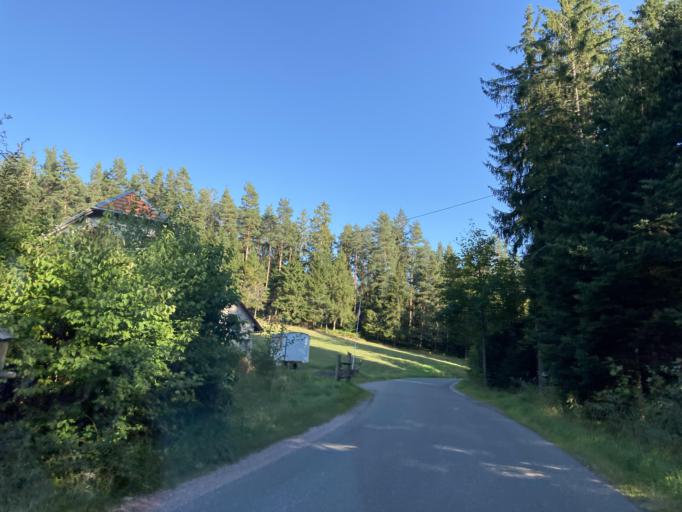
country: DE
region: Baden-Wuerttemberg
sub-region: Freiburg Region
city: Sankt Georgen im Schwarzwald
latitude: 48.1398
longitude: 8.2887
